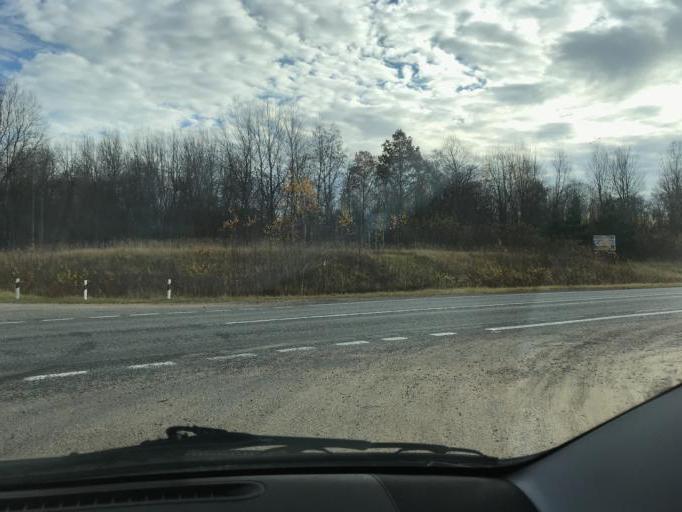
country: BY
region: Vitebsk
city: Haradok
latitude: 55.4580
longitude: 30.0442
